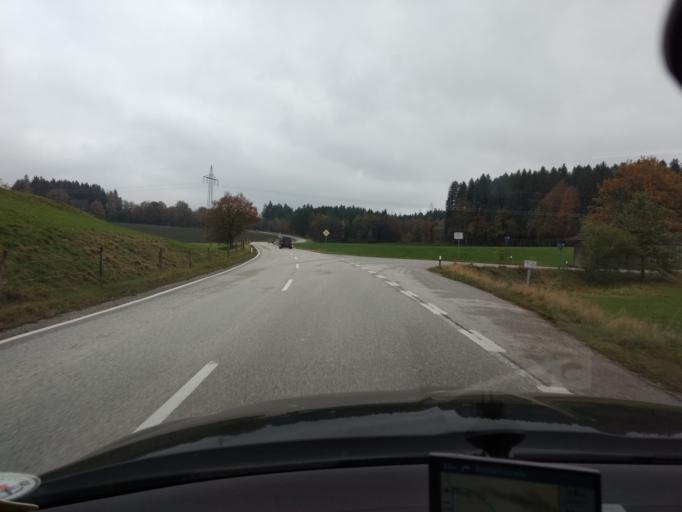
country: DE
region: Bavaria
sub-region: Upper Bavaria
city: Konigsdorf
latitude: 47.8113
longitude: 11.4915
